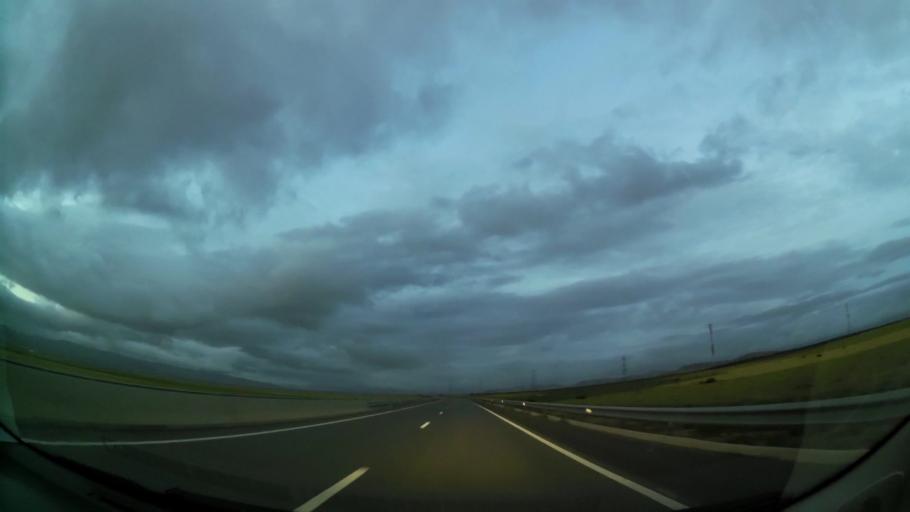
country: MA
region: Oriental
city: El Aioun
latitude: 34.6331
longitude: -2.3314
